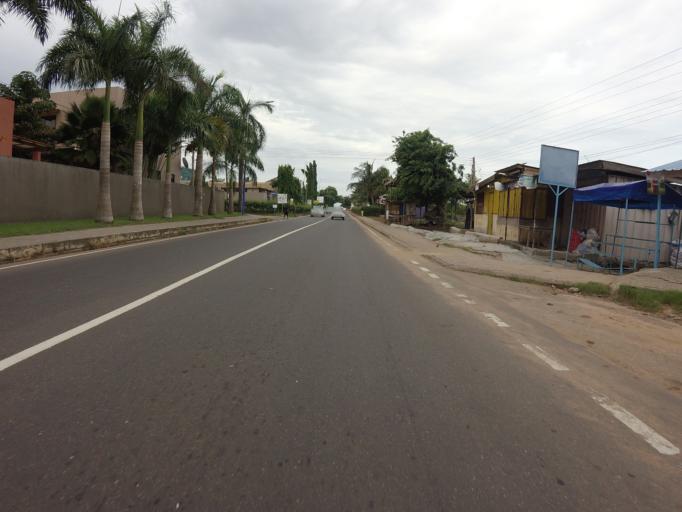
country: GH
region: Greater Accra
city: Dome
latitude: 5.6074
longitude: -0.2152
